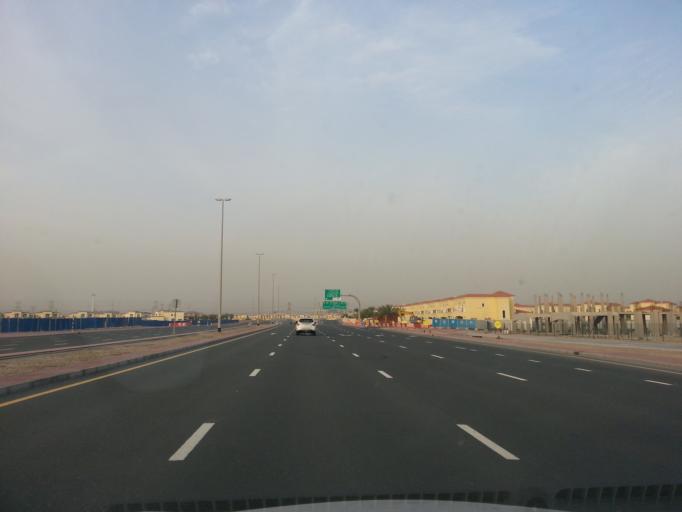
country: AE
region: Dubai
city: Dubai
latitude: 25.0456
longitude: 55.1644
